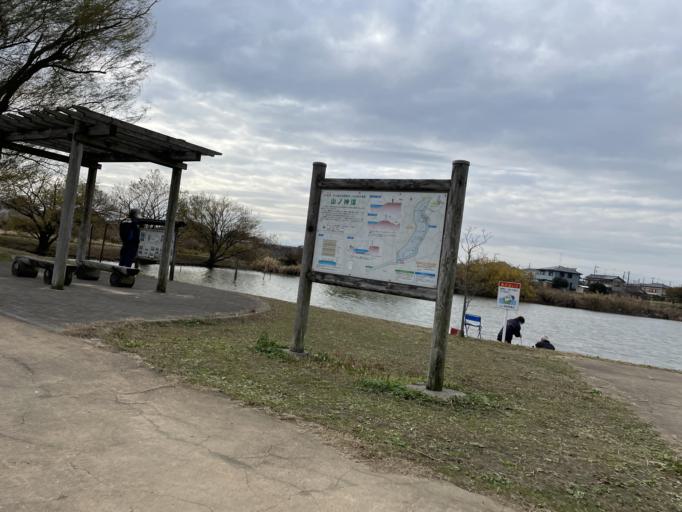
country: JP
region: Saitama
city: Shiraoka
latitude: 36.0205
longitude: 139.6464
